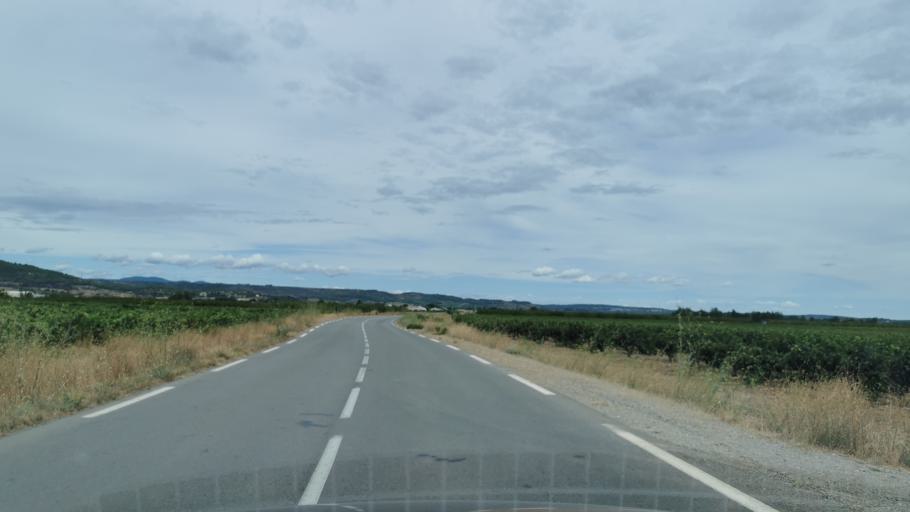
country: FR
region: Languedoc-Roussillon
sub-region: Departement de l'Aude
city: Argeliers
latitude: 43.2942
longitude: 2.9041
